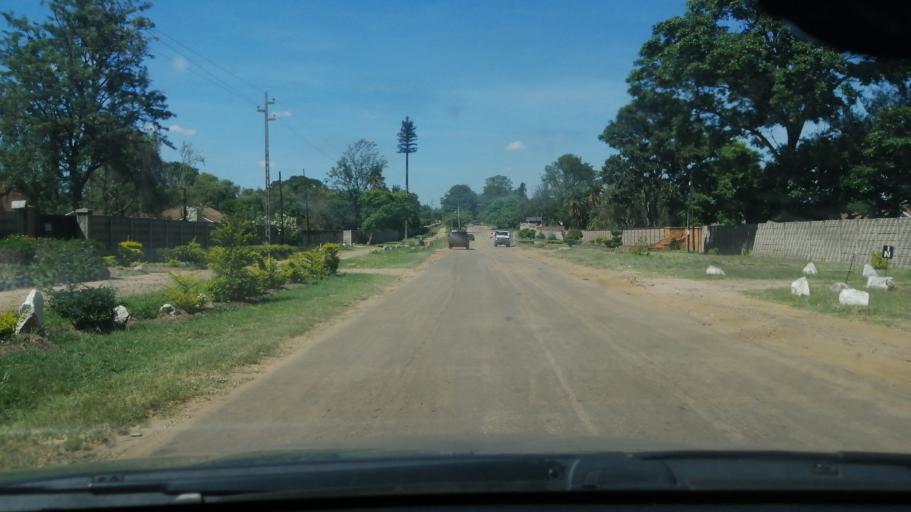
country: ZW
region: Harare
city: Epworth
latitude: -17.8203
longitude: 31.1292
